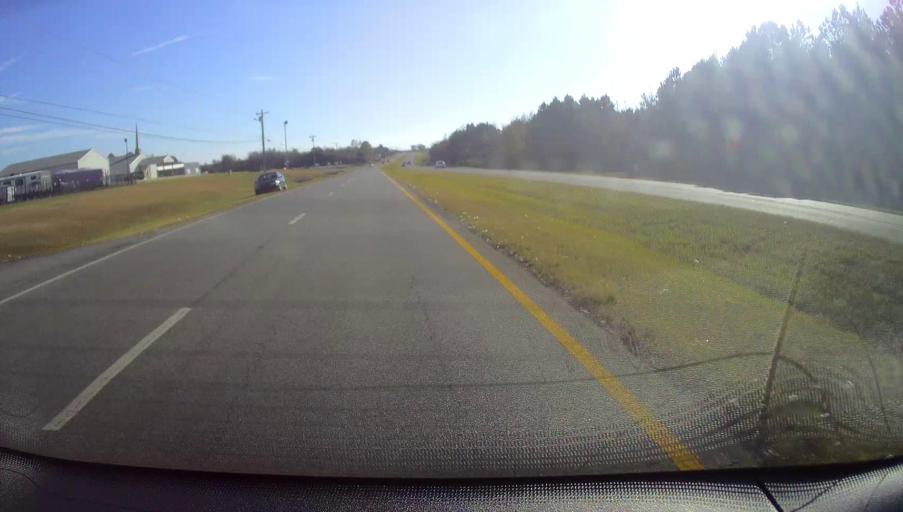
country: US
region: Alabama
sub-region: Limestone County
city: Athens
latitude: 34.7147
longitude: -86.9561
